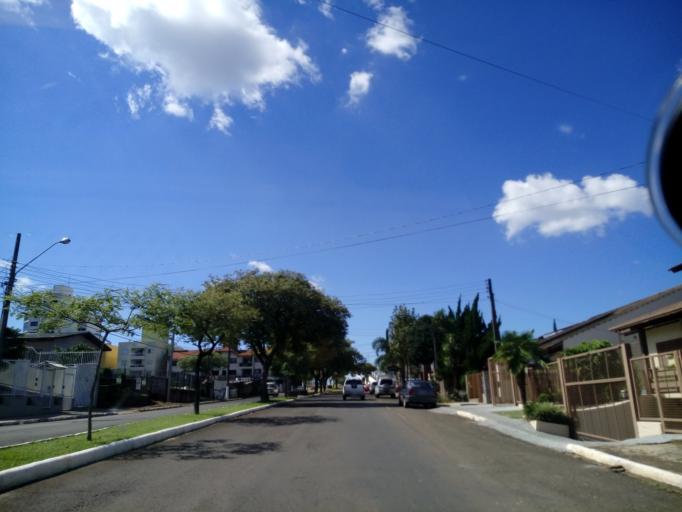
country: BR
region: Santa Catarina
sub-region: Chapeco
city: Chapeco
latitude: -27.1123
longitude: -52.6156
